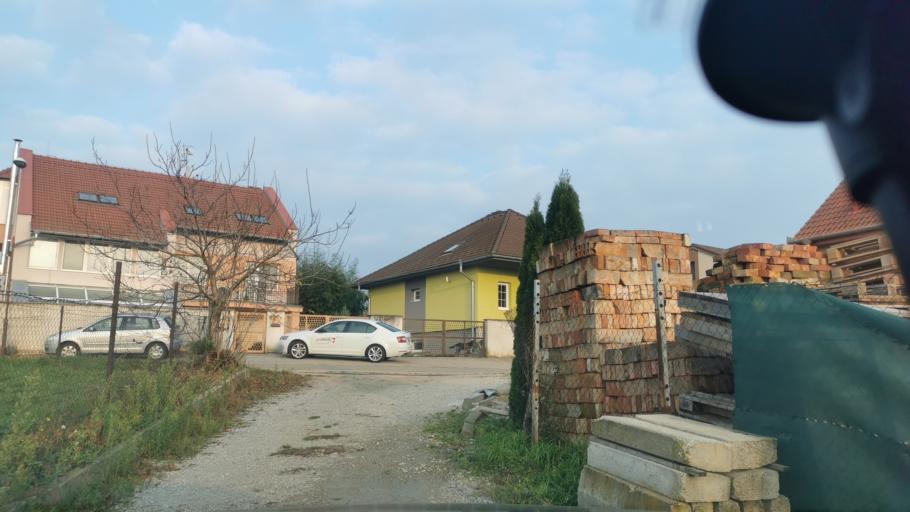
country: SK
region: Trnavsky
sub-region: Okres Skalica
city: Skalica
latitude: 48.7879
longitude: 17.2203
